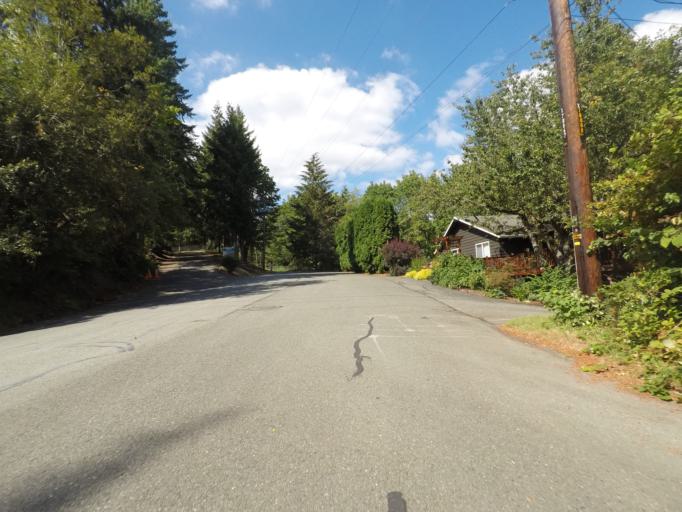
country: US
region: Washington
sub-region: King County
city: Lake Forest Park
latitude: 47.7626
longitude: -122.2653
